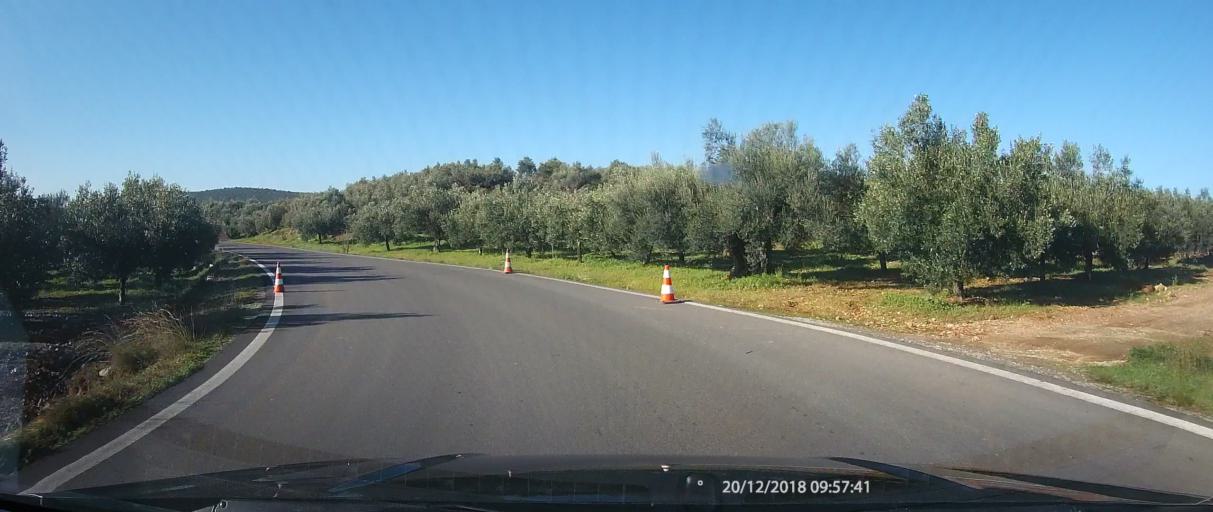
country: GR
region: Peloponnese
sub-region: Nomos Lakonias
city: Yerakion
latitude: 37.0236
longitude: 22.5932
